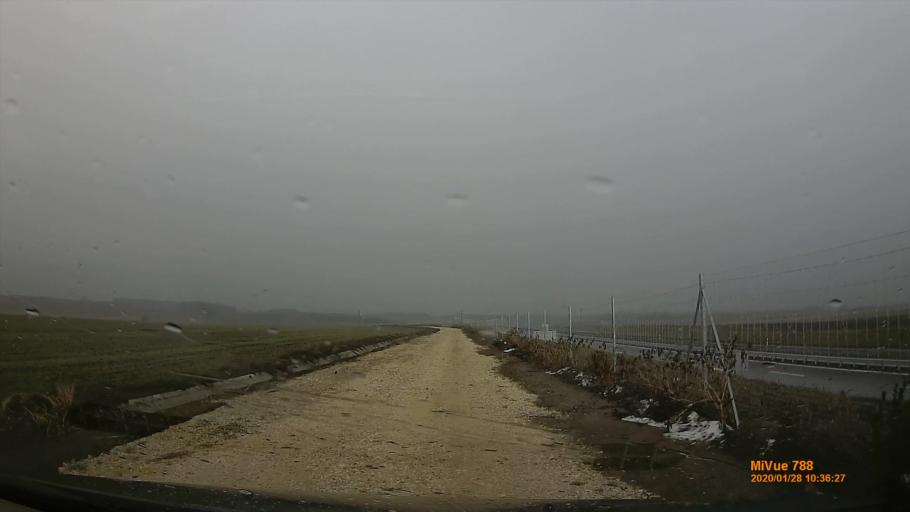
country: HU
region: Pest
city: Monor
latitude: 47.3556
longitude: 19.4884
